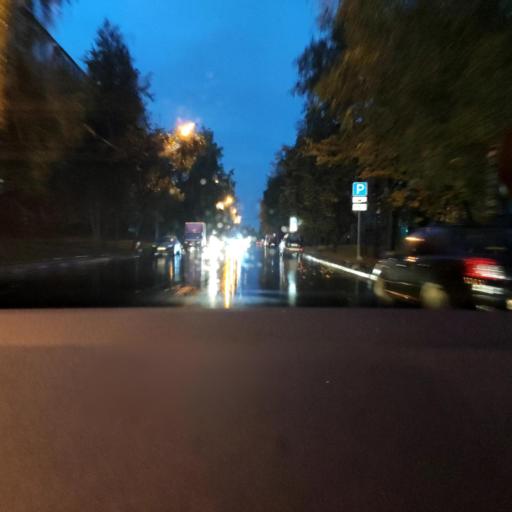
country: RU
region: Moskovskaya
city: Razvilka
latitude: 55.6028
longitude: 37.7357
